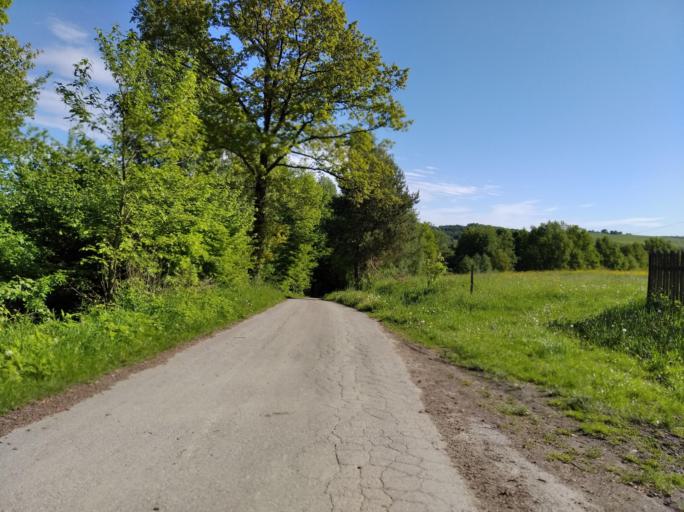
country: PL
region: Subcarpathian Voivodeship
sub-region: Powiat strzyzowski
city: Frysztak
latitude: 49.8408
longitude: 21.5609
